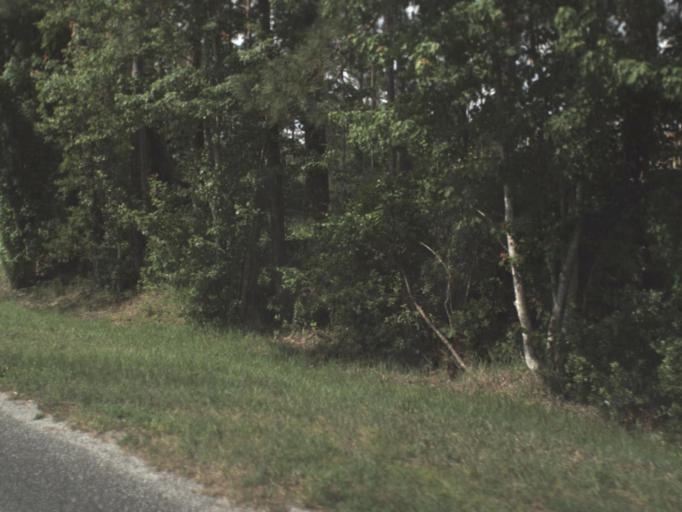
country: US
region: Florida
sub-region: Saint Johns County
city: Saint Augustine Shores
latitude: 29.7870
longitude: -81.3182
